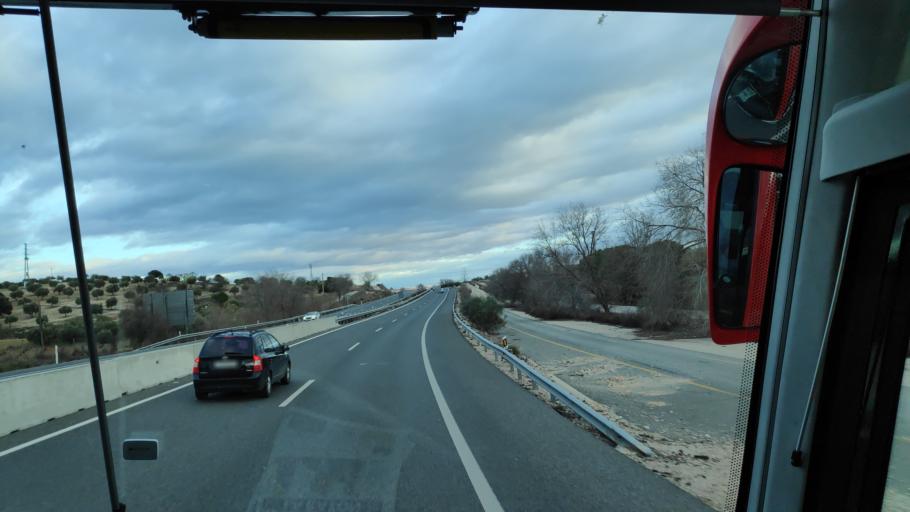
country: ES
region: Madrid
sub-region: Provincia de Madrid
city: Villarejo de Salvanes
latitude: 40.1556
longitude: -3.2533
